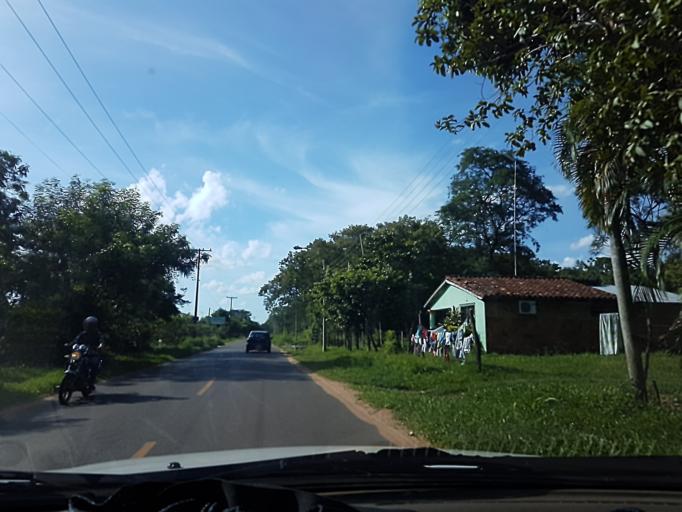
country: PY
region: Central
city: Limpio
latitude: -25.1946
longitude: -57.4600
